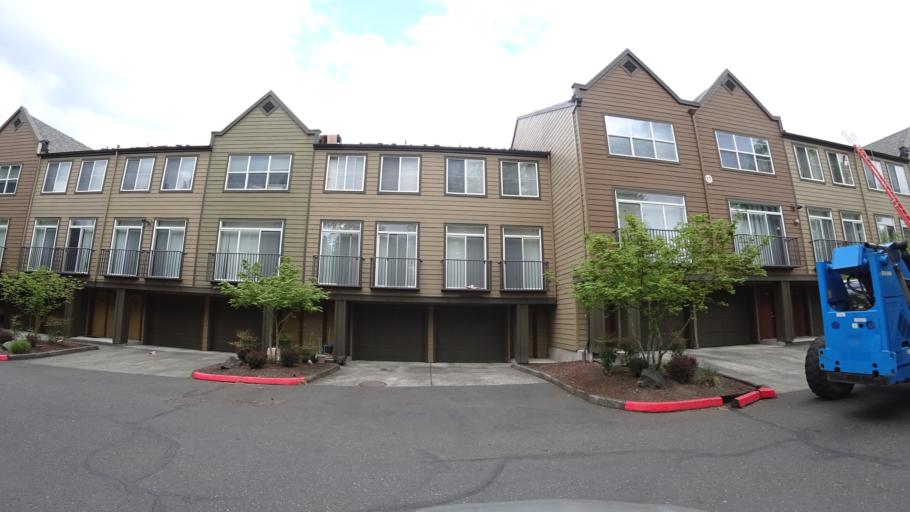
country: US
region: Oregon
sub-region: Washington County
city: Rockcreek
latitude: 45.5427
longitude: -122.8858
